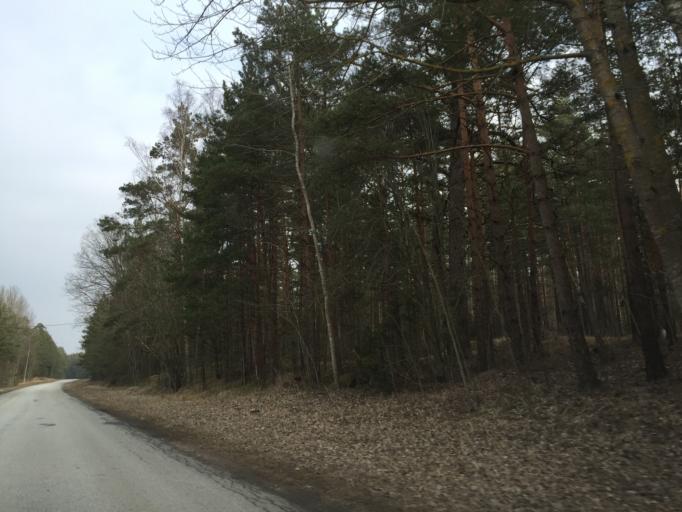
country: LV
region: Salacgrivas
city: Ainazi
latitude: 57.9568
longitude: 24.3999
